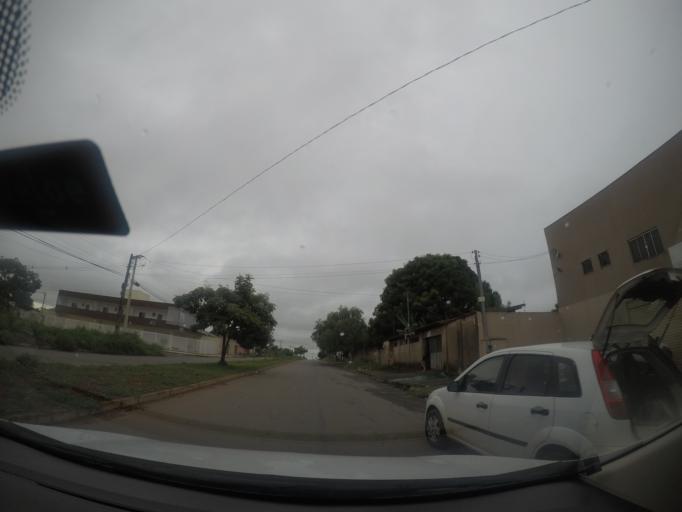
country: BR
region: Goias
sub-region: Goiania
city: Goiania
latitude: -16.7527
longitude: -49.3174
